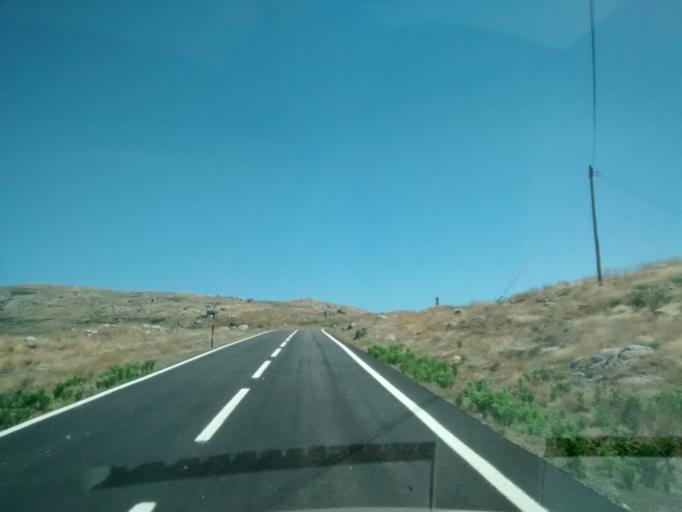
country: PT
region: Guarda
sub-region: Seia
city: Seia
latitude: 40.4092
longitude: -7.6562
